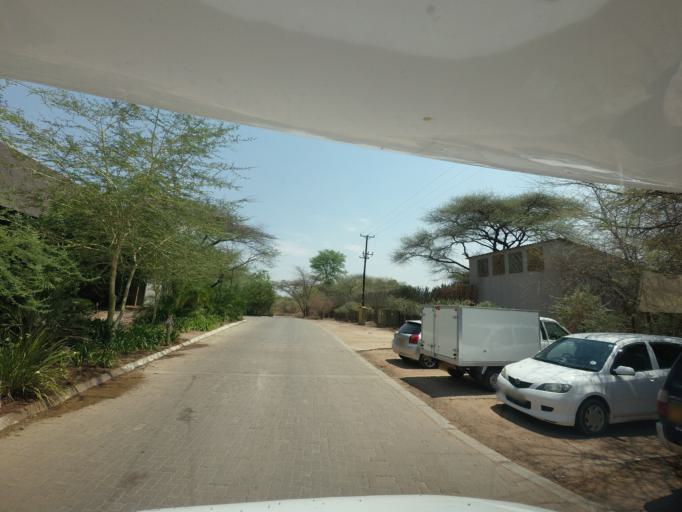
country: BW
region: North West
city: Kasane
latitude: -17.8071
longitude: 25.1470
